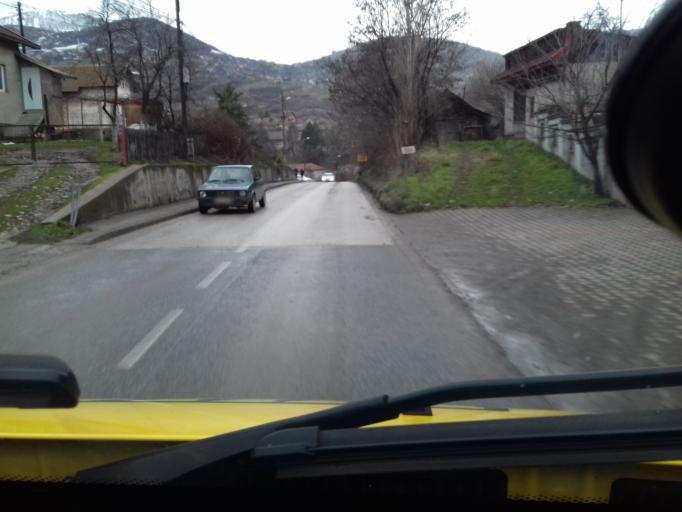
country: BA
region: Federation of Bosnia and Herzegovina
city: Zenica
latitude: 44.2298
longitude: 17.8892
